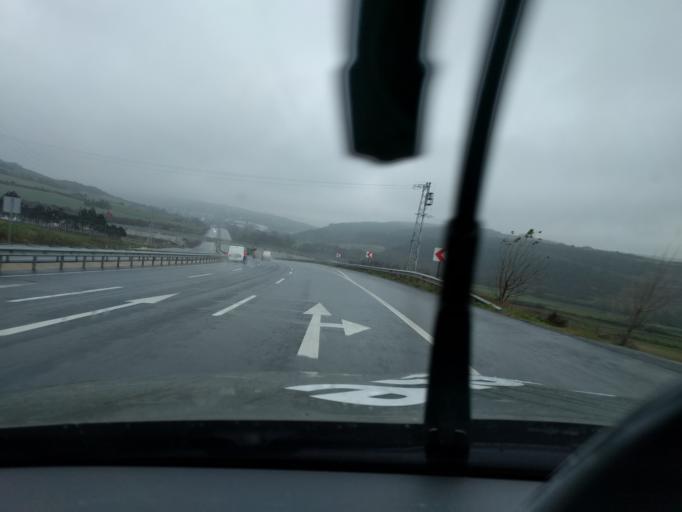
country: TR
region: Istanbul
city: Boyalik
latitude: 41.2280
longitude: 28.5387
